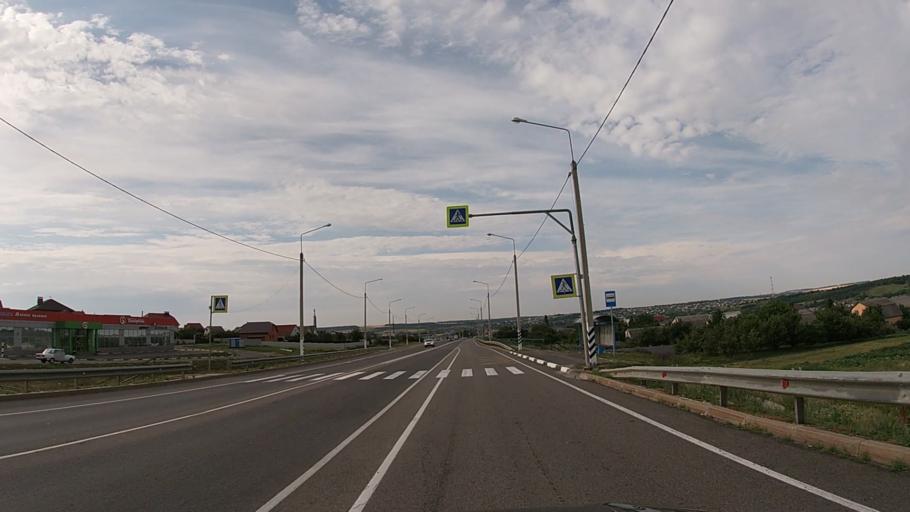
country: RU
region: Belgorod
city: Severnyy
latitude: 50.6466
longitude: 36.4682
